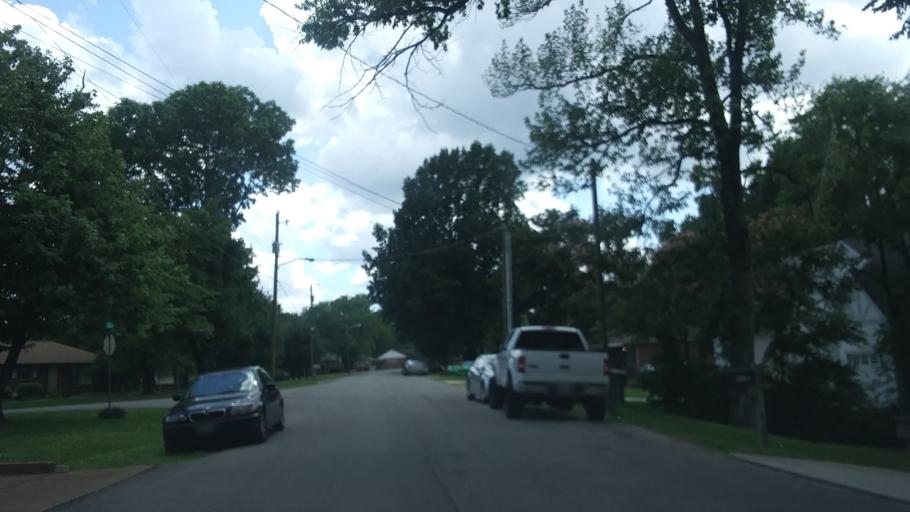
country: US
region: Tennessee
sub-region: Davidson County
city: Oak Hill
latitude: 36.0722
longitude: -86.7060
